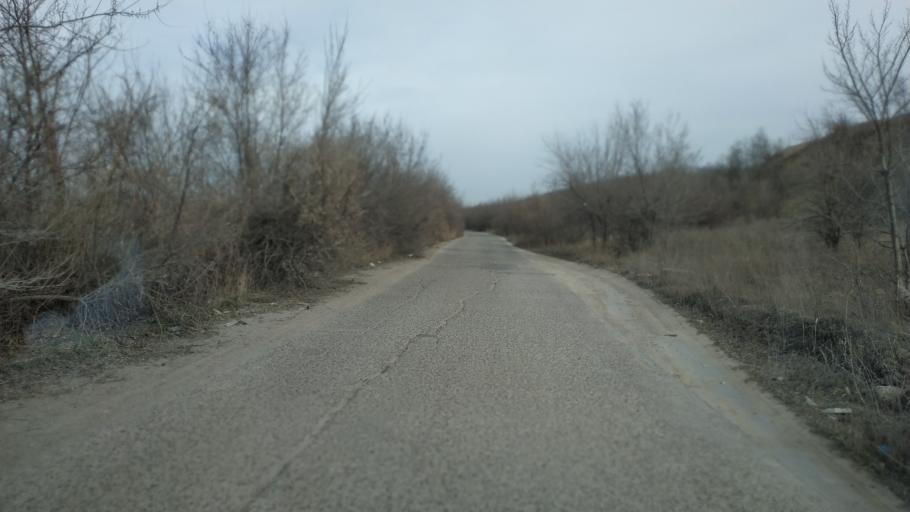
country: MD
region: Chisinau
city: Vatra
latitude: 47.0814
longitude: 28.7417
